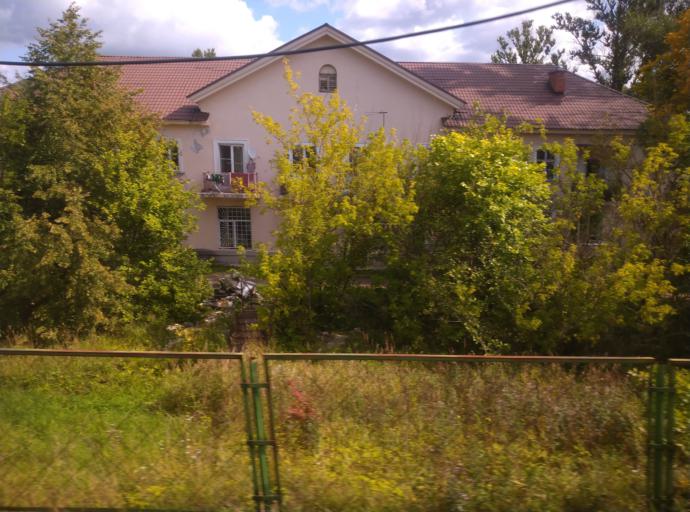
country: RU
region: Leningrad
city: Ul'yanovka
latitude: 59.6372
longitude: 30.7555
